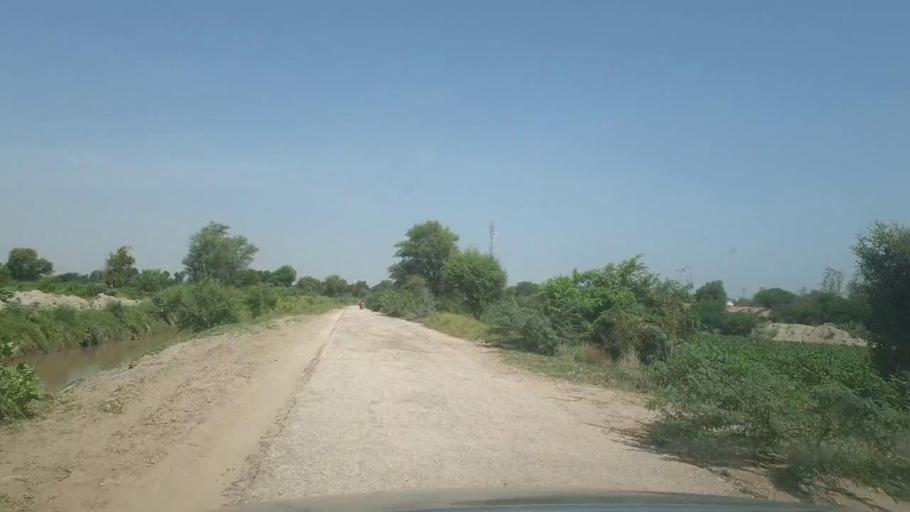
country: PK
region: Sindh
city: Khairpur
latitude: 27.4020
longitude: 69.0371
